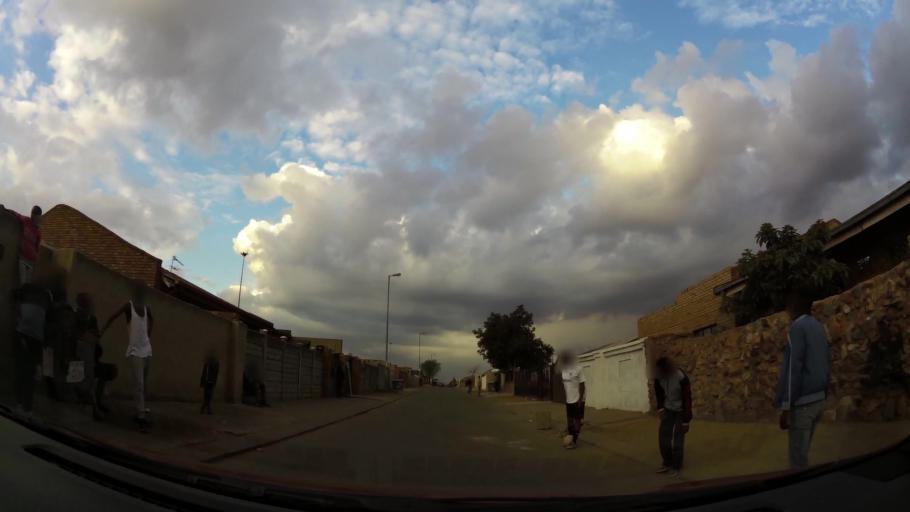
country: ZA
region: Gauteng
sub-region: City of Johannesburg Metropolitan Municipality
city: Soweto
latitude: -26.2482
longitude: 27.8266
